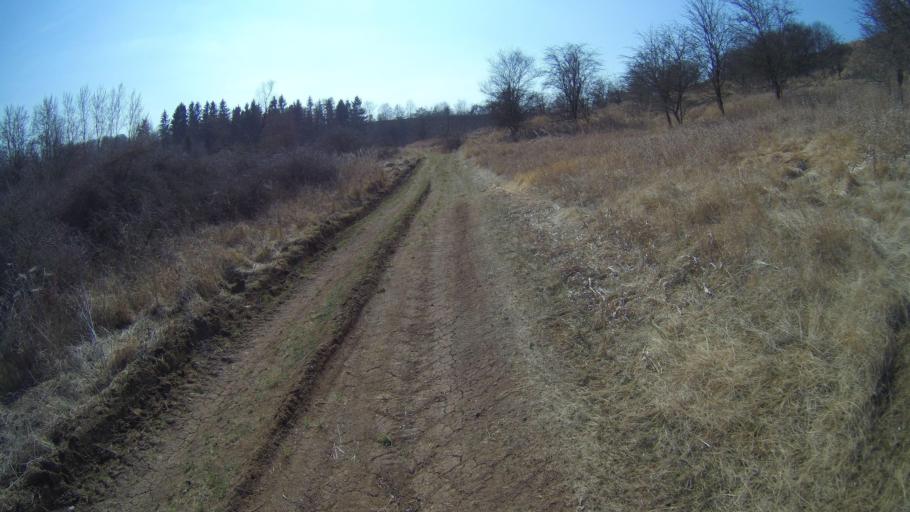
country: CZ
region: Ustecky
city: Mecholupy
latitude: 50.2554
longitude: 13.5442
